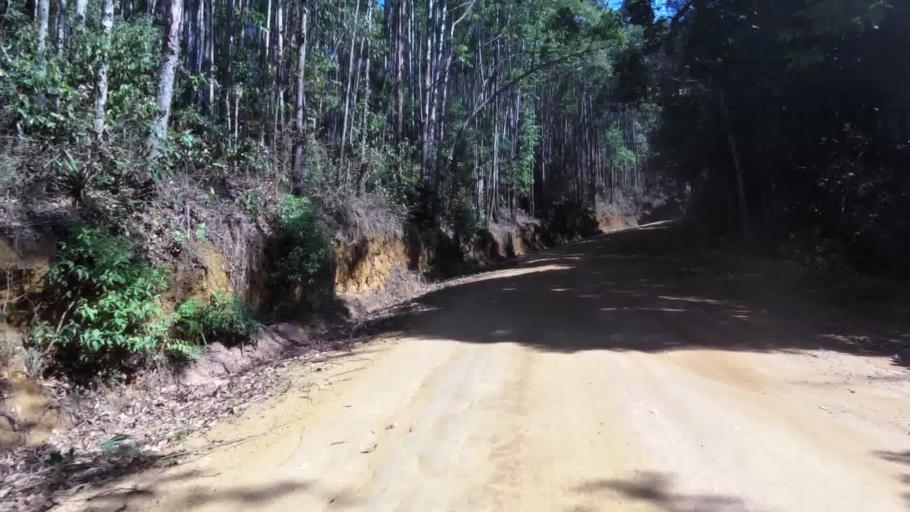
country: BR
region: Espirito Santo
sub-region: Alfredo Chaves
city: Alfredo Chaves
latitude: -20.5193
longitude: -40.8730
